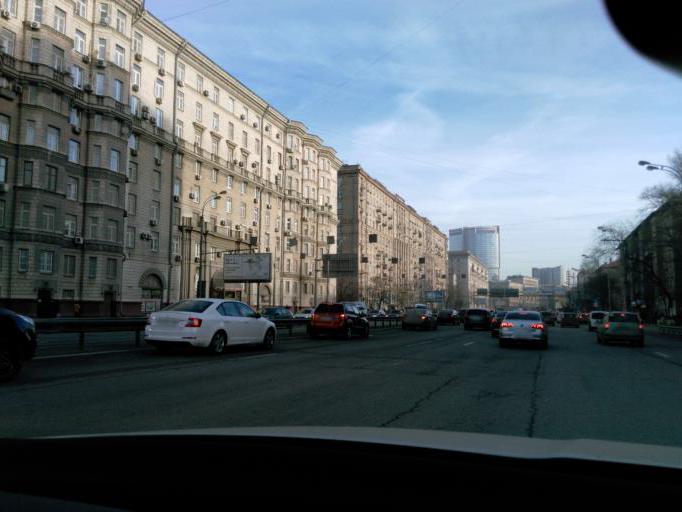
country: RU
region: Moskovskaya
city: Presnenskiy
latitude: 55.7761
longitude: 37.5551
